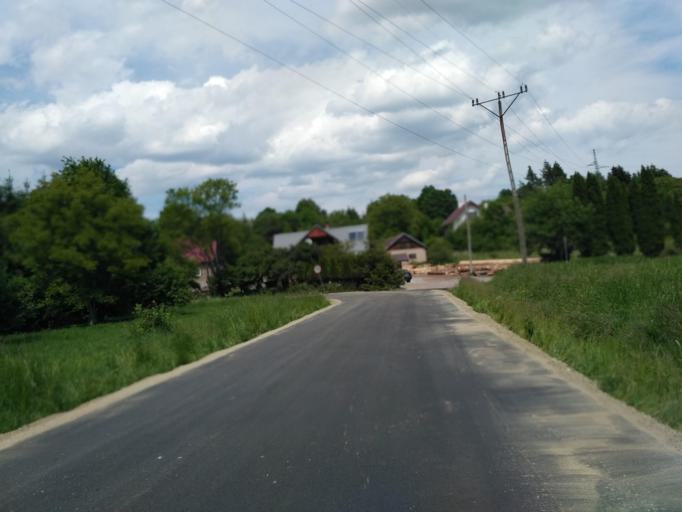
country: PL
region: Subcarpathian Voivodeship
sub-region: Powiat krosnienski
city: Odrzykon
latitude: 49.7119
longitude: 21.7452
